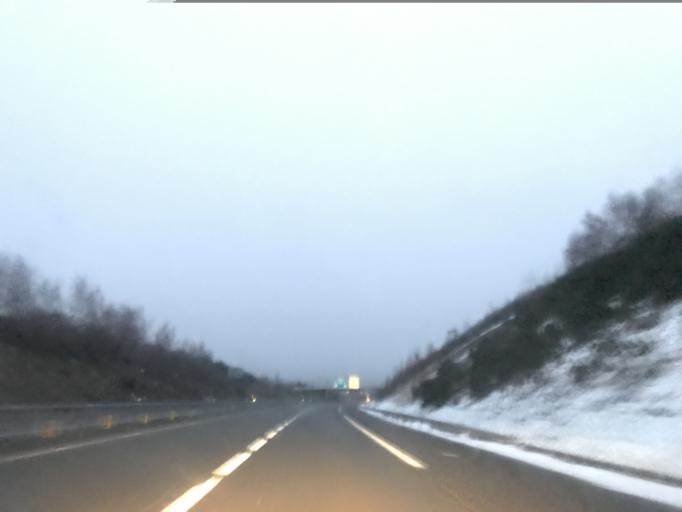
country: FR
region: Auvergne
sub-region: Departement du Puy-de-Dome
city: Gelles
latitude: 45.8316
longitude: 2.8110
